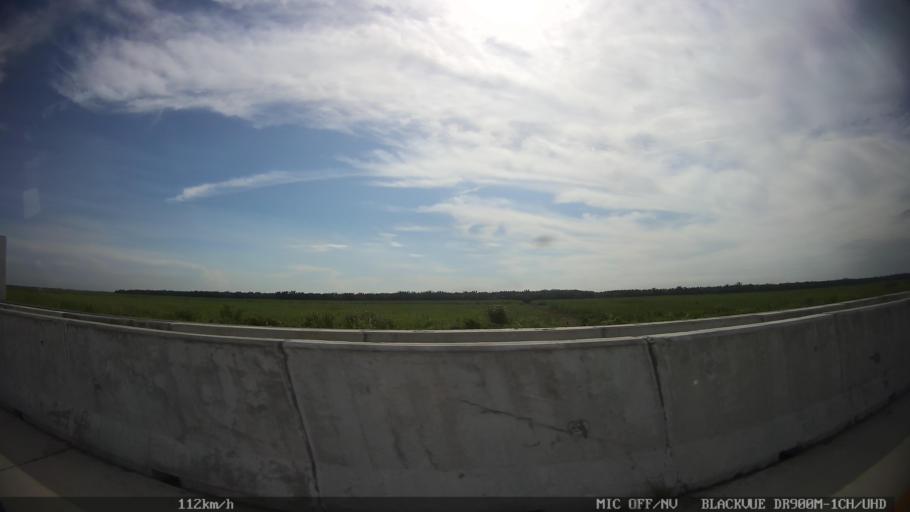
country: ID
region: North Sumatra
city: Binjai
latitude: 3.6577
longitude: 98.5335
